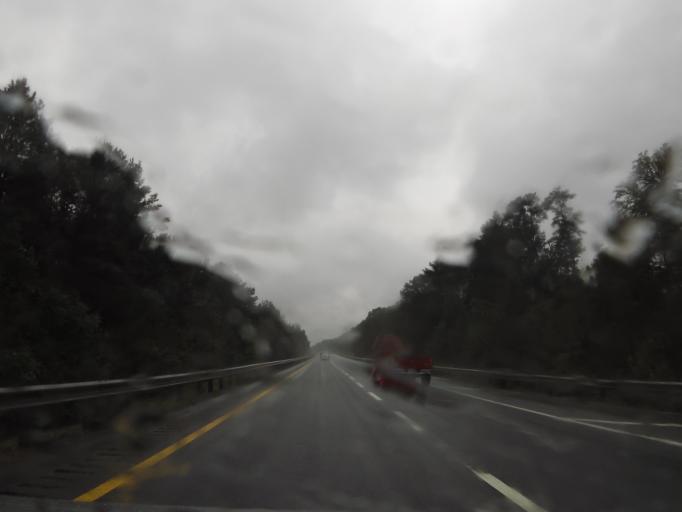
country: US
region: Tennessee
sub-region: Bradley County
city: Hopewell
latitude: 35.2620
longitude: -84.8326
